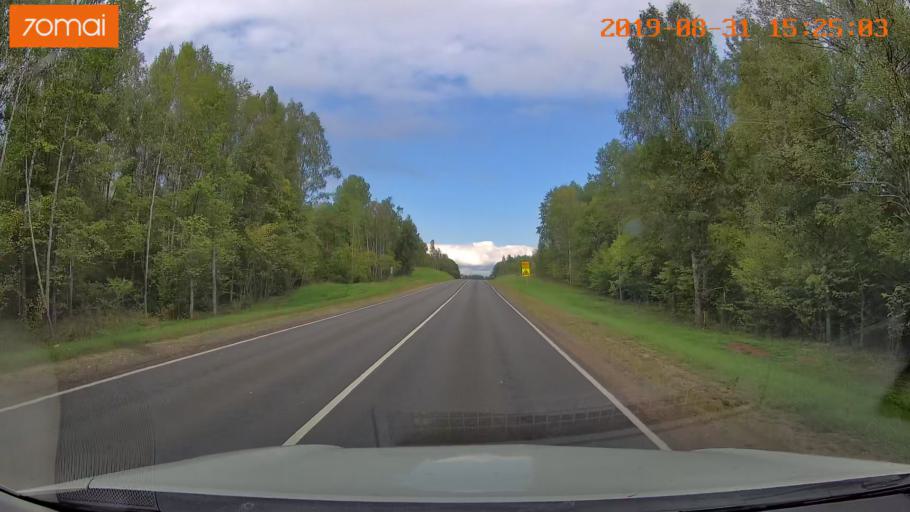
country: RU
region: Kaluga
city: Baryatino
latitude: 54.5359
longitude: 34.5137
